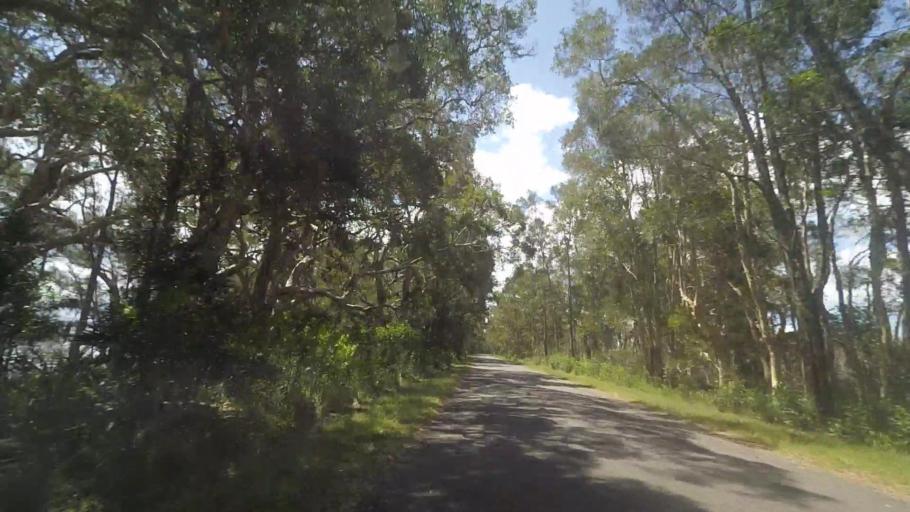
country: AU
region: New South Wales
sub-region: Great Lakes
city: Bulahdelah
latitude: -32.5212
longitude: 152.3227
